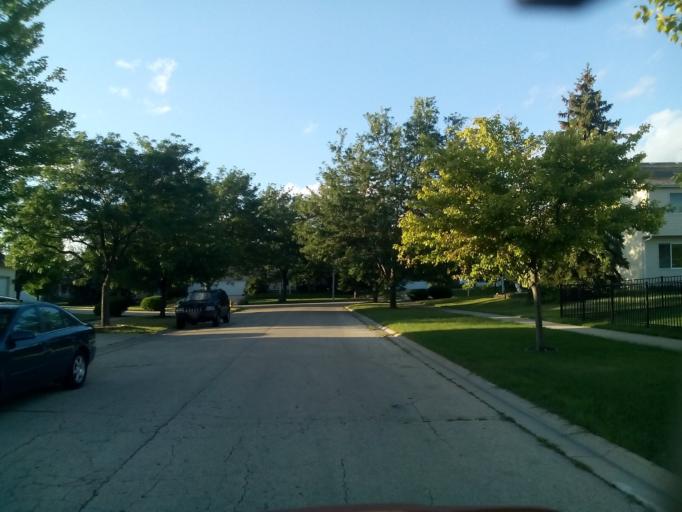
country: US
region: Illinois
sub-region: Will County
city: Bolingbrook
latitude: 41.6963
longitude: -88.1348
